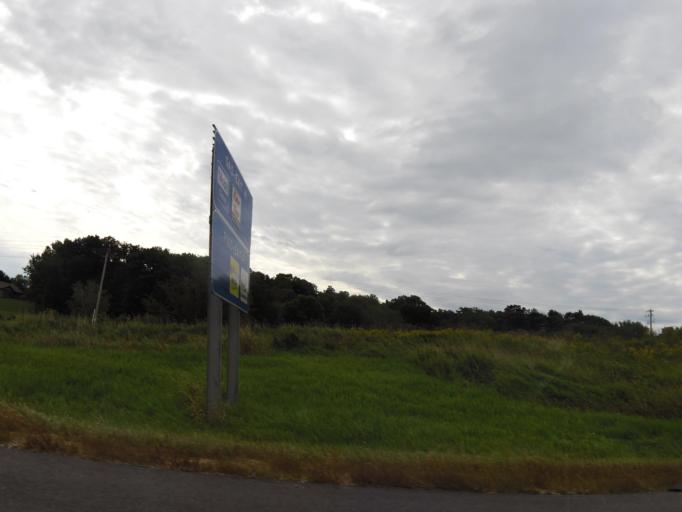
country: US
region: Wisconsin
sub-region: Monroe County
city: Tomah
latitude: 43.9534
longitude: -90.5137
